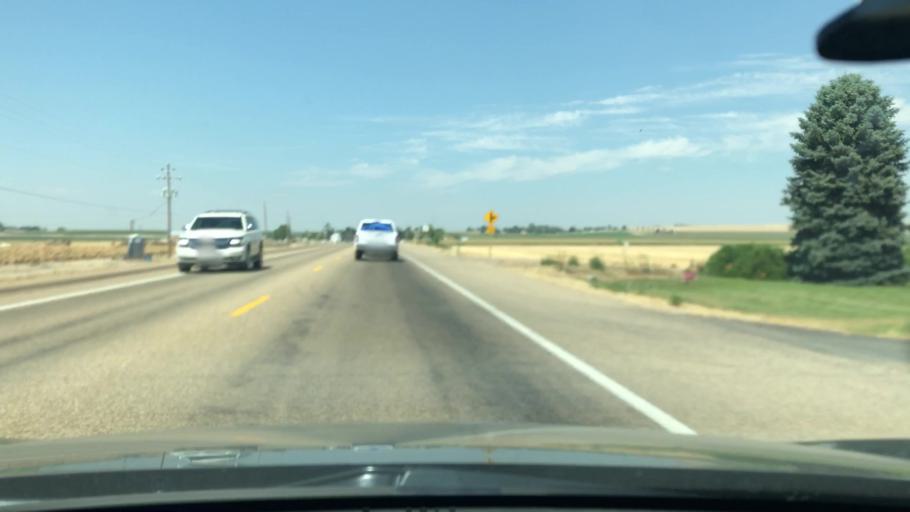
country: US
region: Idaho
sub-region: Canyon County
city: Parma
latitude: 43.8005
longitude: -116.9522
